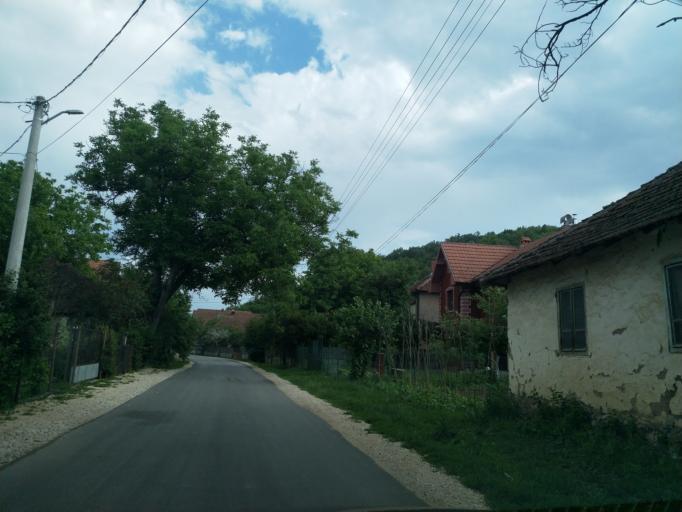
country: RS
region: Central Serbia
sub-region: Borski Okrug
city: Bor
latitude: 44.0166
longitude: 21.9816
